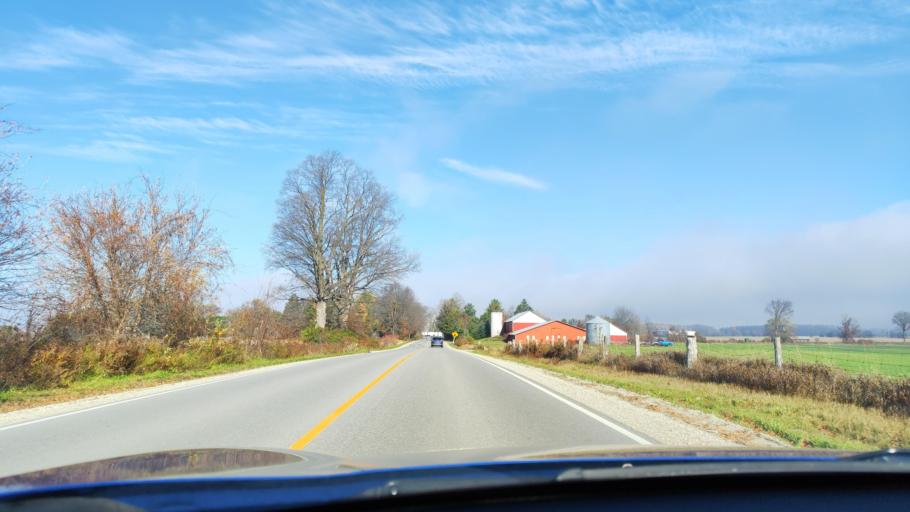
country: CA
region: Ontario
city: Wasaga Beach
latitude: 44.4190
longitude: -80.0621
